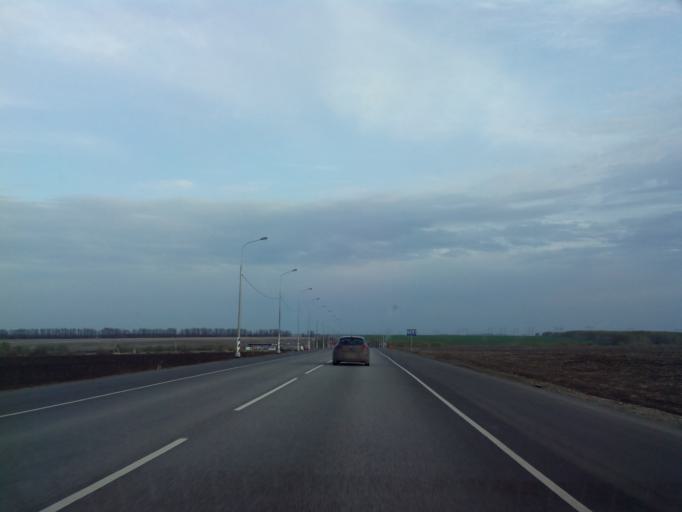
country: RU
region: Rjazan
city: Ryazhsk
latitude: 53.5616
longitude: 40.0511
